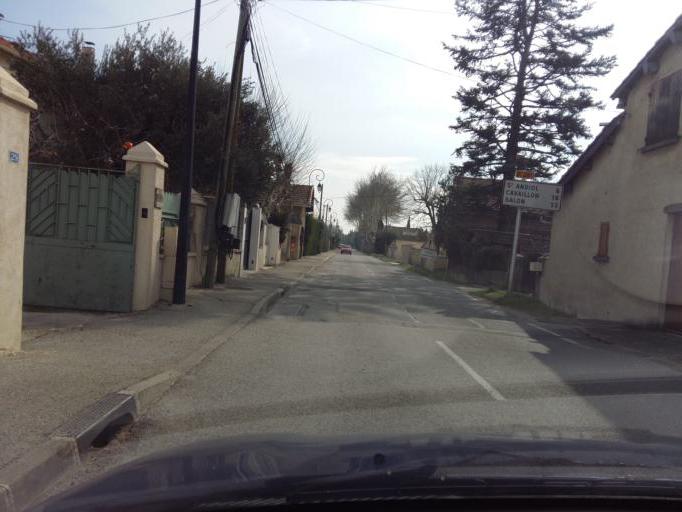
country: FR
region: Provence-Alpes-Cote d'Azur
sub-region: Departement des Bouches-du-Rhone
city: Noves
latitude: 43.8747
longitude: 4.9026
